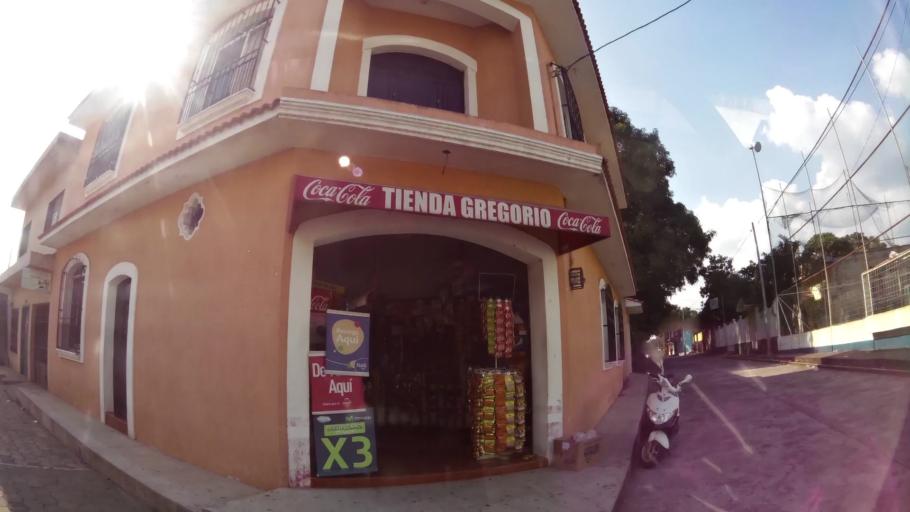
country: GT
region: Retalhuleu
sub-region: Municipio de Retalhuleu
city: Retalhuleu
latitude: 14.5413
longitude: -91.6849
